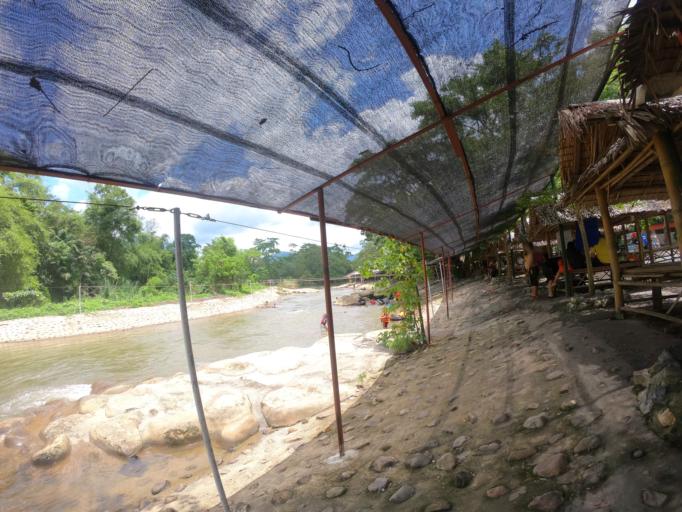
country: TH
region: Nakhon Nayok
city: Nakhon Nayok
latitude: 14.3100
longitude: 101.3128
